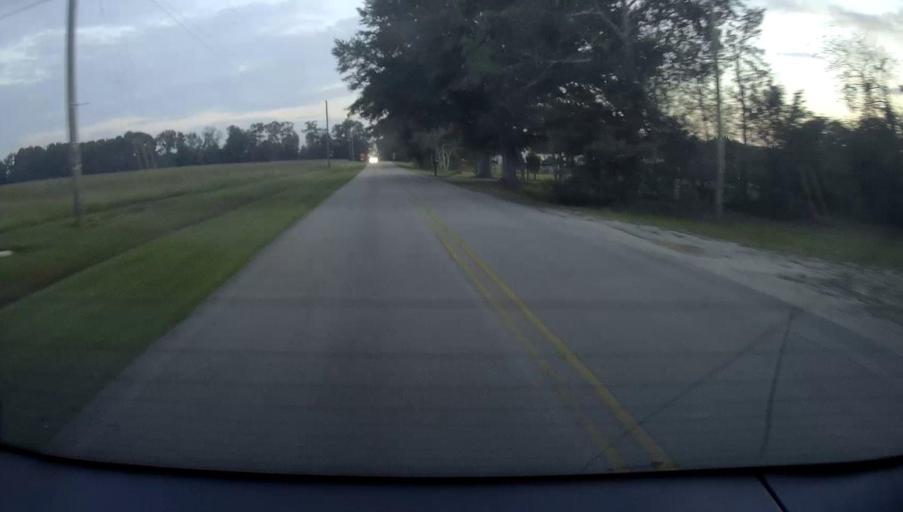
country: US
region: Georgia
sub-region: Henry County
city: Locust Grove
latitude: 33.3260
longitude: -84.0427
